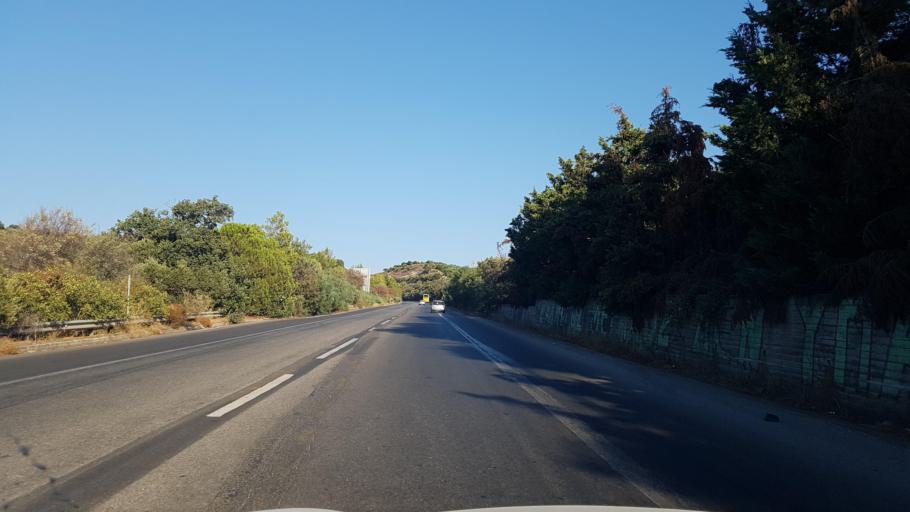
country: GR
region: Crete
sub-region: Nomos Chanias
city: Gerani
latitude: 35.5158
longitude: 23.8273
